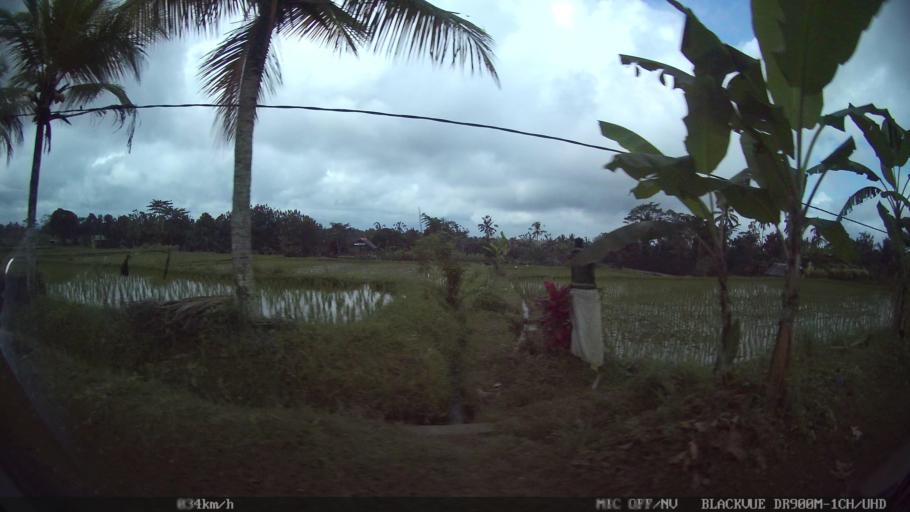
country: ID
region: Bali
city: Badung
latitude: -8.4213
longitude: 115.2273
